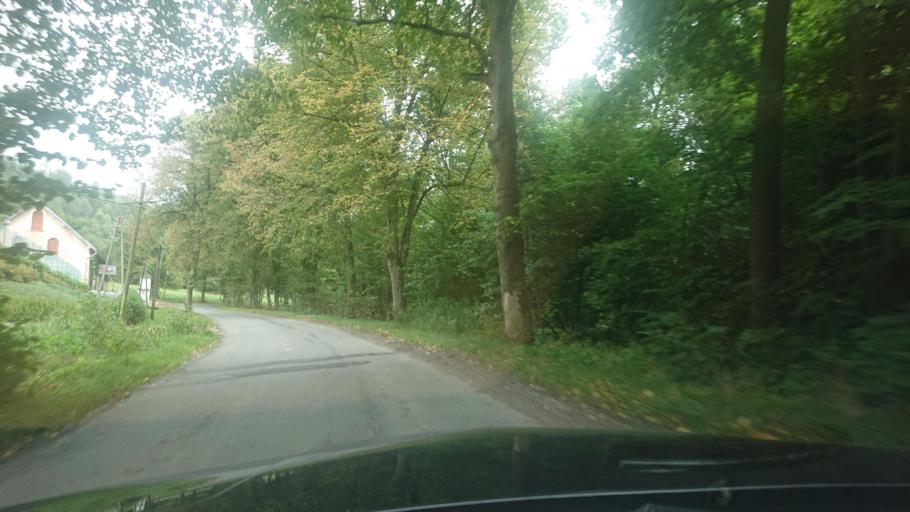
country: PL
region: Lower Silesian Voivodeship
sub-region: Powiat klodzki
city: Bystrzyca Klodzka
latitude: 50.3204
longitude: 16.7236
